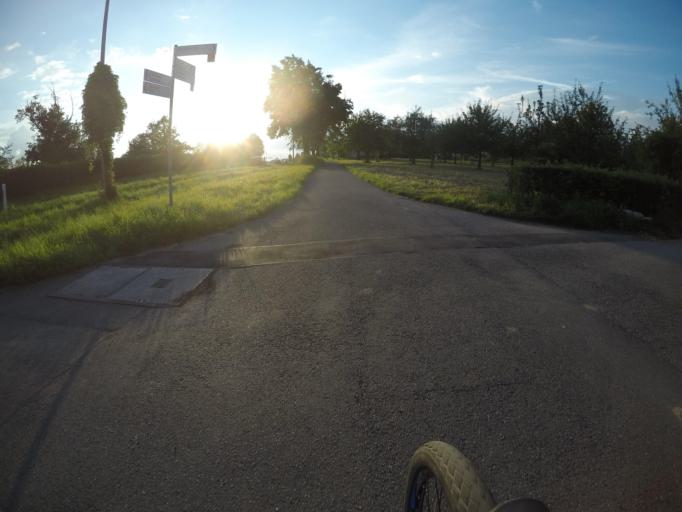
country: DE
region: Baden-Wuerttemberg
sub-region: Regierungsbezirk Stuttgart
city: Ostfildern
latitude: 48.7348
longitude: 9.2411
